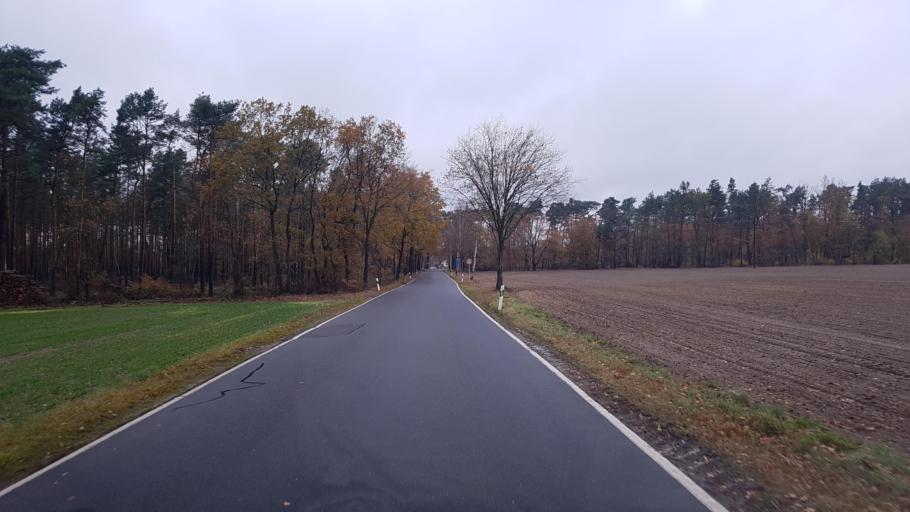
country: DE
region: Brandenburg
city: Drebkau
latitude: 51.6915
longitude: 14.1989
